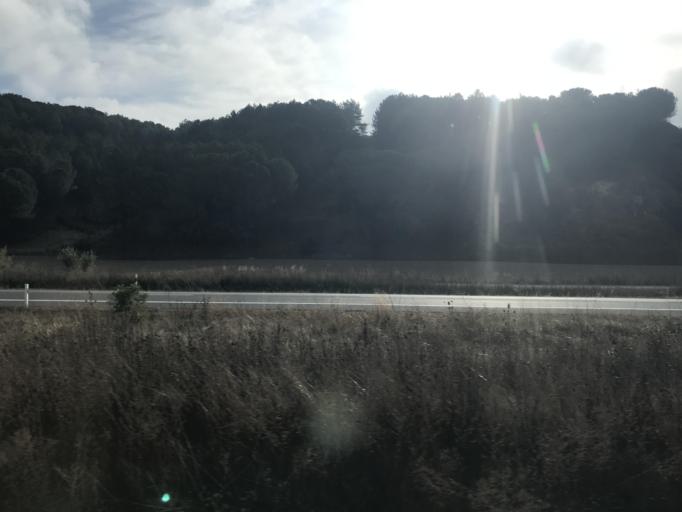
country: ES
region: Castille and Leon
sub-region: Provincia de Burgos
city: Pradanos de Bureba
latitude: 42.5060
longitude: -3.3432
